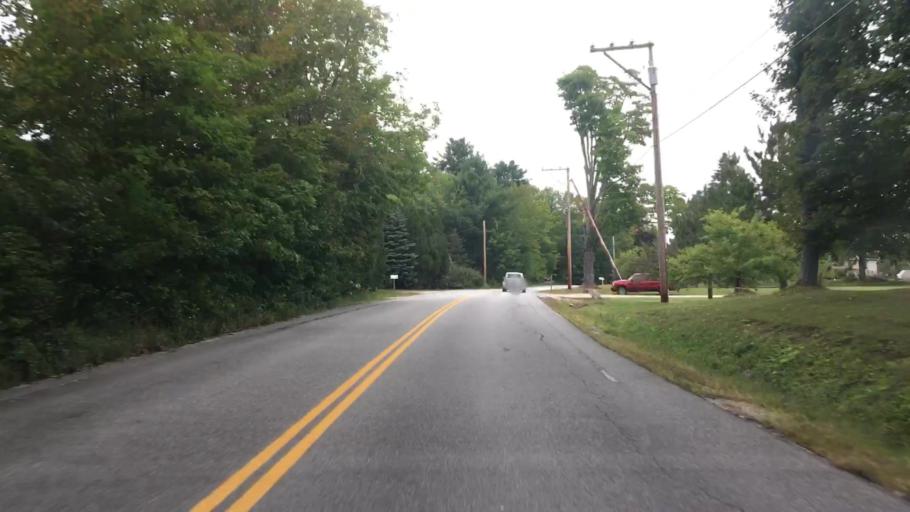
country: US
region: Maine
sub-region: Cumberland County
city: Yarmouth
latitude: 43.8461
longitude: -70.2137
